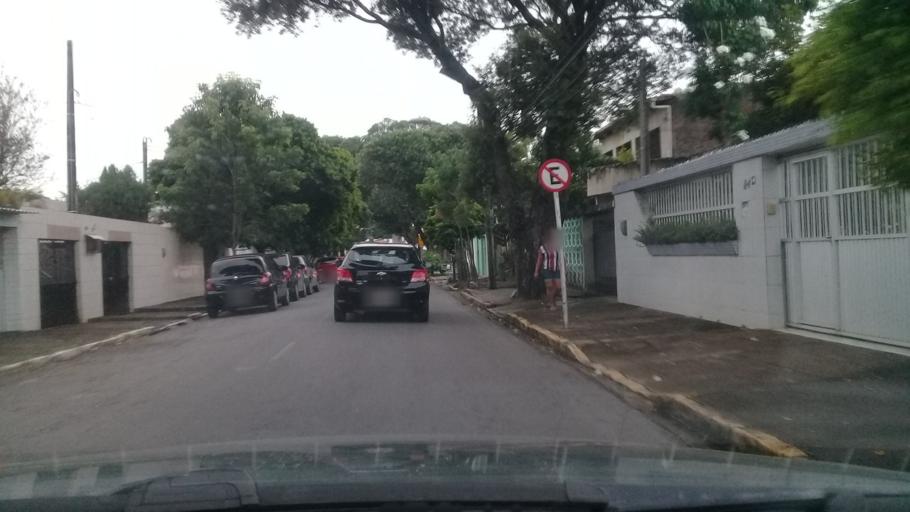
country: BR
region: Pernambuco
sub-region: Recife
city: Recife
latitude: -8.1140
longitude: -34.9239
